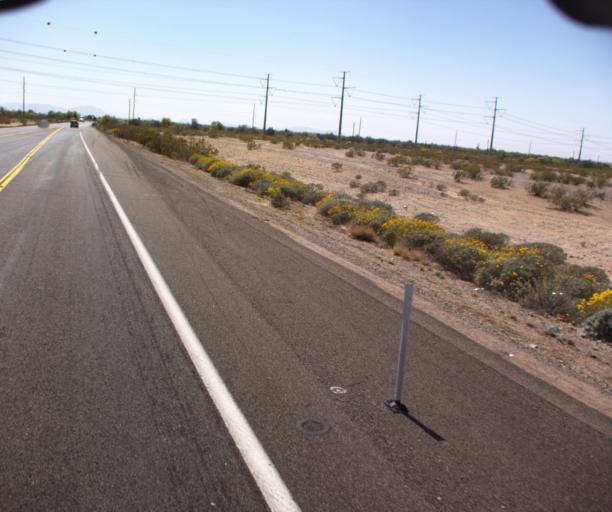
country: US
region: Arizona
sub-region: Maricopa County
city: Gila Bend
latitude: 32.9739
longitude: -112.6716
